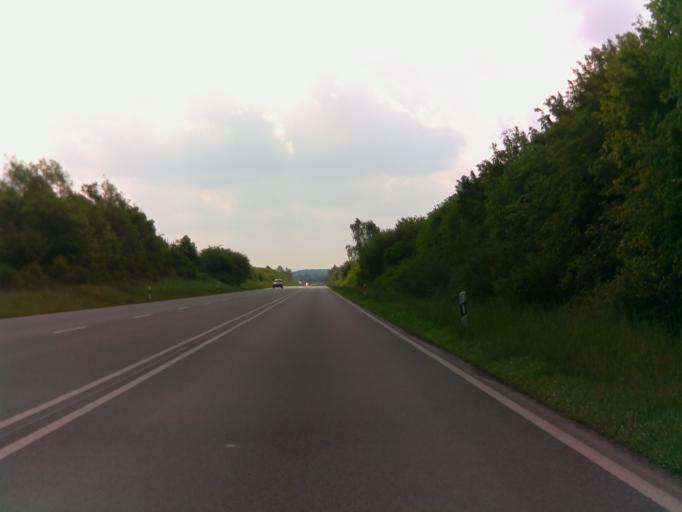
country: DE
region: Saxony-Anhalt
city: Gardelegen
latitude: 52.5373
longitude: 11.4175
